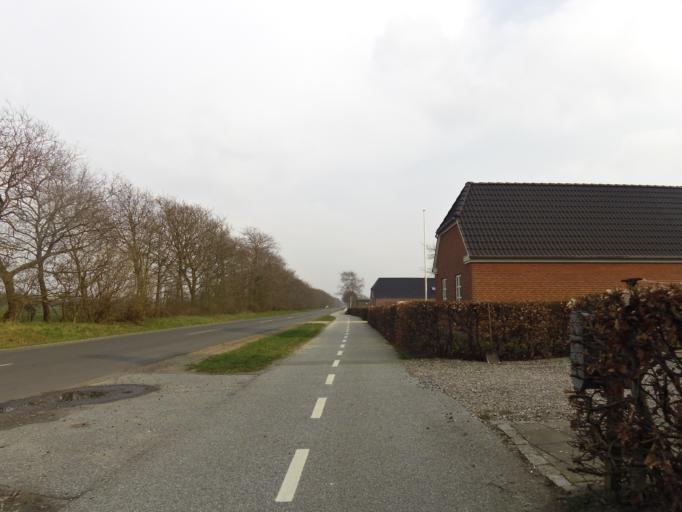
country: DK
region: South Denmark
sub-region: Esbjerg Kommune
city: Ribe
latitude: 55.3467
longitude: 8.7512
